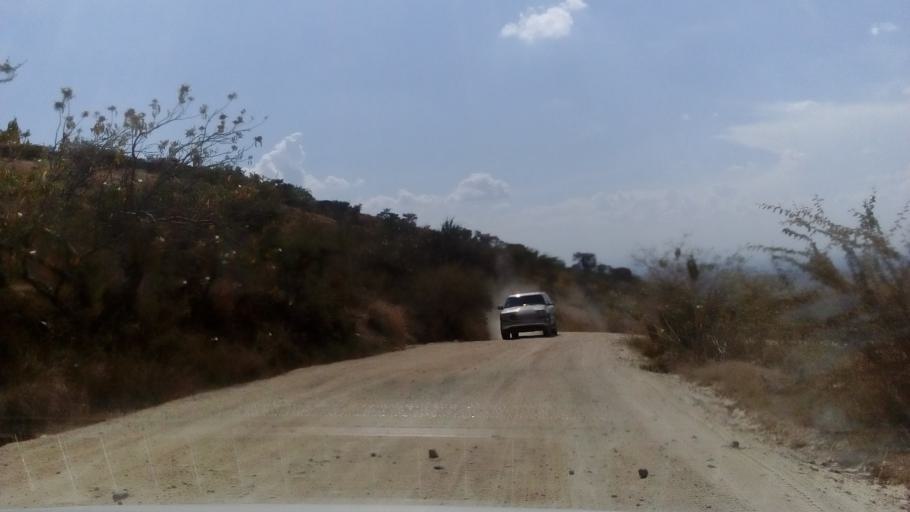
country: MX
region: Guanajuato
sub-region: Silao de la Victoria
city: Loma de Yerbabuena
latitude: 21.0808
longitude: -101.4495
